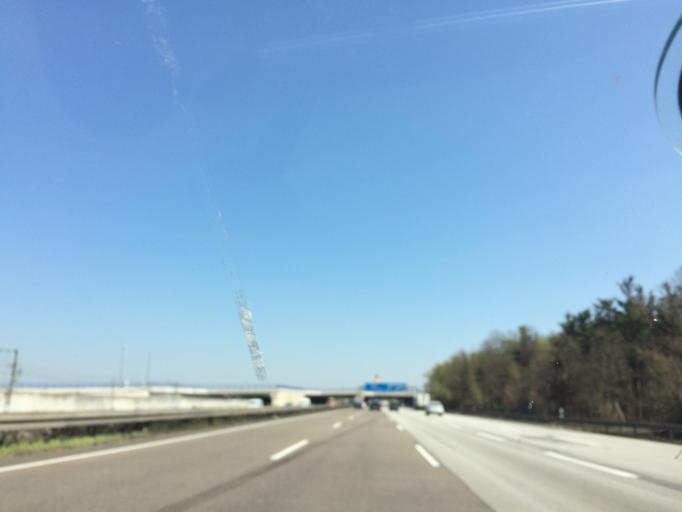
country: DE
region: Hesse
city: Kelsterbach
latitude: 50.0420
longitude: 8.5327
